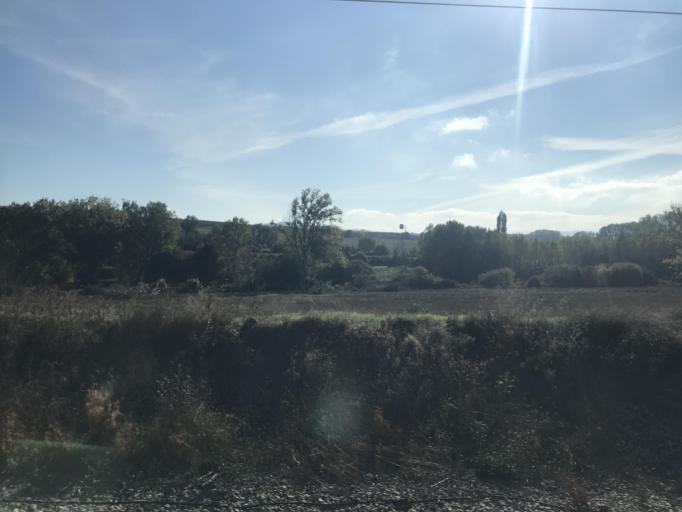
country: ES
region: Basque Country
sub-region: Provincia de Alava
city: Arminon
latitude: 42.7772
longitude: -2.8288
